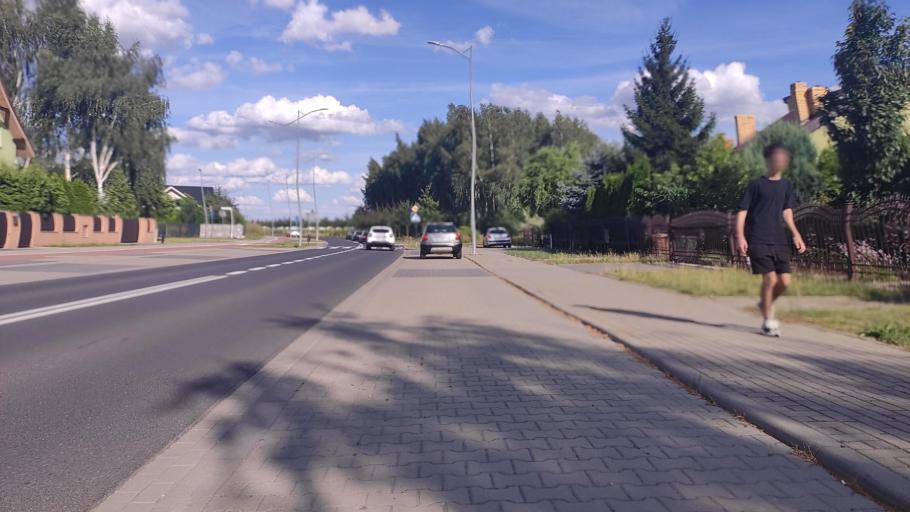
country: PL
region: Greater Poland Voivodeship
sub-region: Powiat poznanski
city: Swarzedz
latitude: 52.3958
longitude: 17.0831
